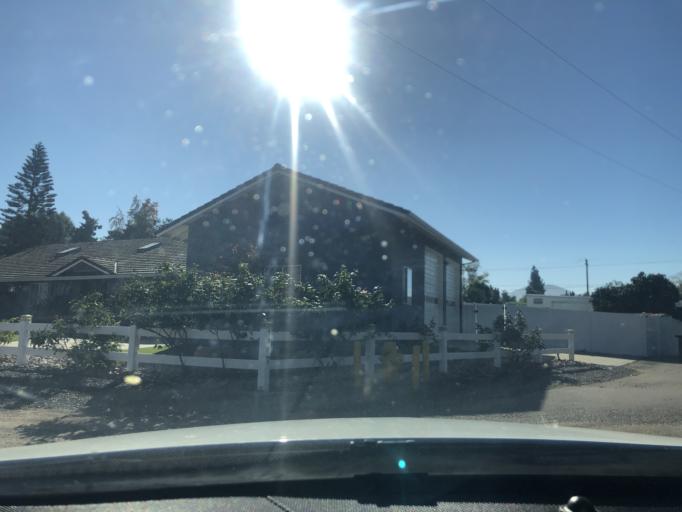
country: US
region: California
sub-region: San Diego County
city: Rancho San Diego
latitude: 32.7724
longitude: -116.9383
